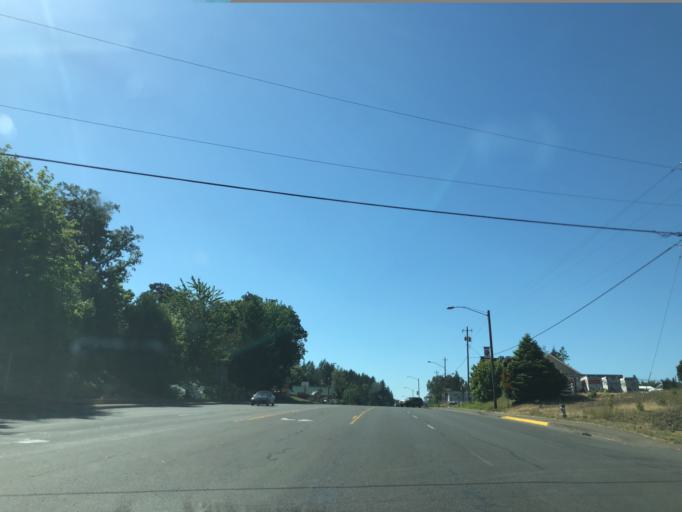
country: US
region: Oregon
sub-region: Linn County
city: Sweet Home
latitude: 44.3986
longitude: -122.7391
